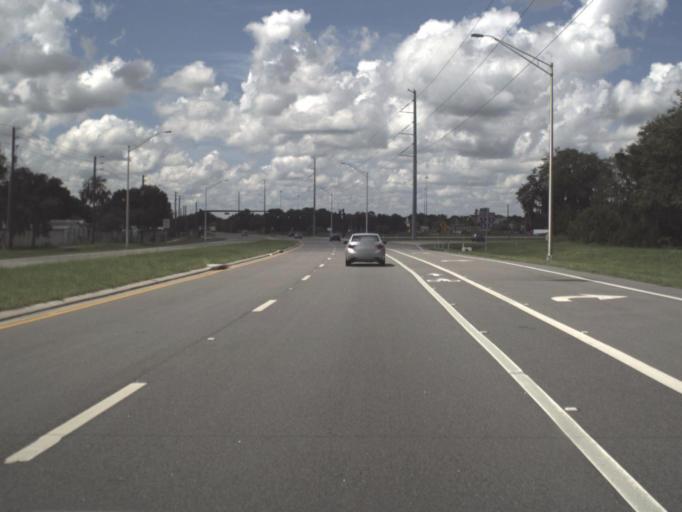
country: US
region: Florida
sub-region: Polk County
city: Gibsonia
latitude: 28.1055
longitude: -81.9416
